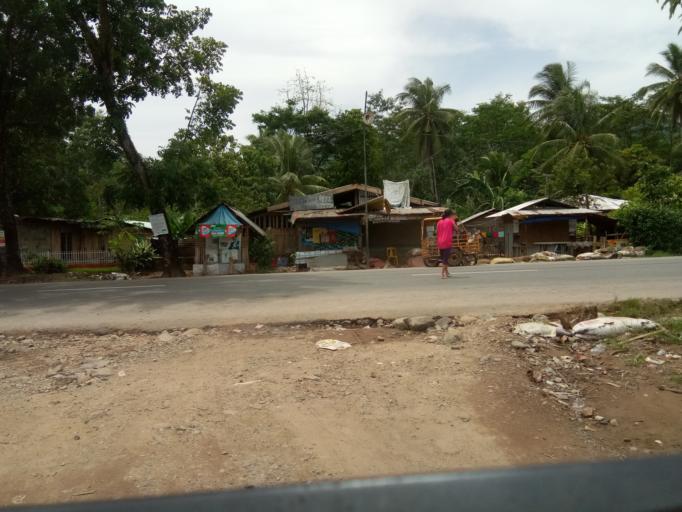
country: PH
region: Caraga
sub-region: Province of Surigao del Norte
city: Alegria
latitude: 9.4969
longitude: 125.5802
